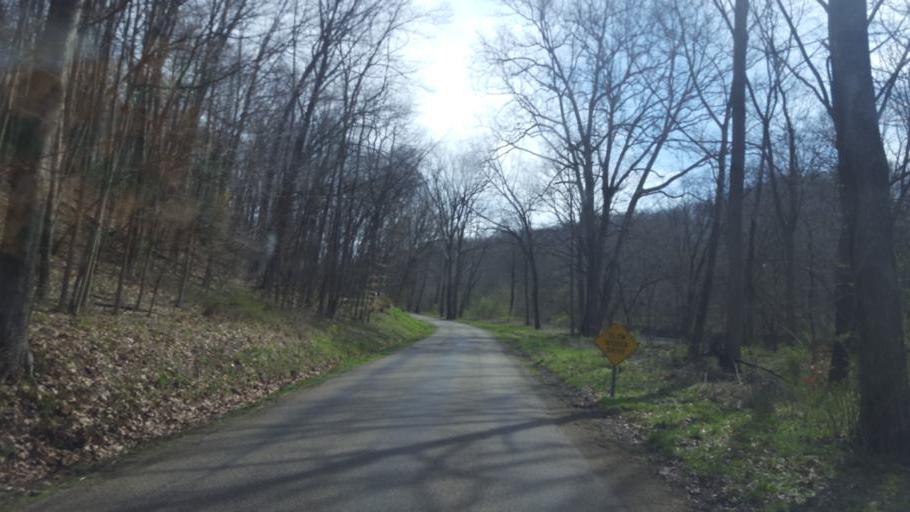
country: US
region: Ohio
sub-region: Knox County
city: Gambier
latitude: 40.3773
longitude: -82.4381
